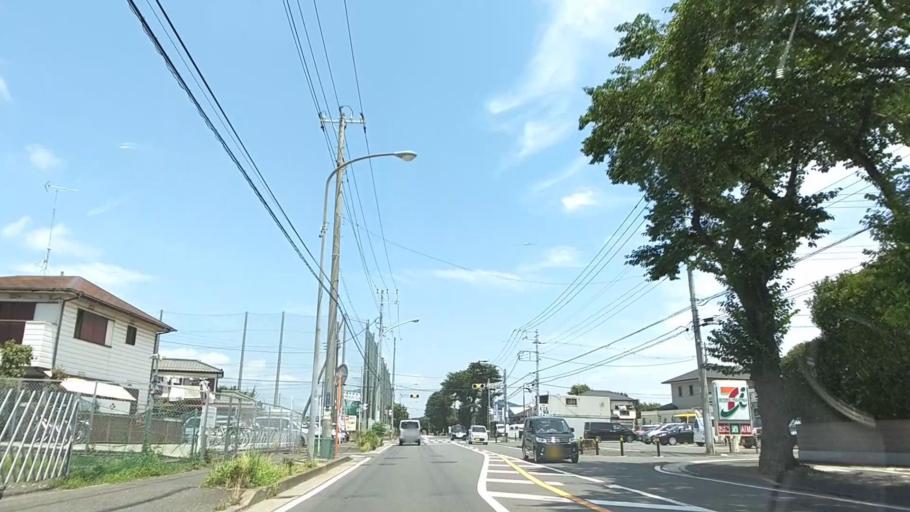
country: JP
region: Kanagawa
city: Minami-rinkan
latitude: 35.4803
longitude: 139.4805
